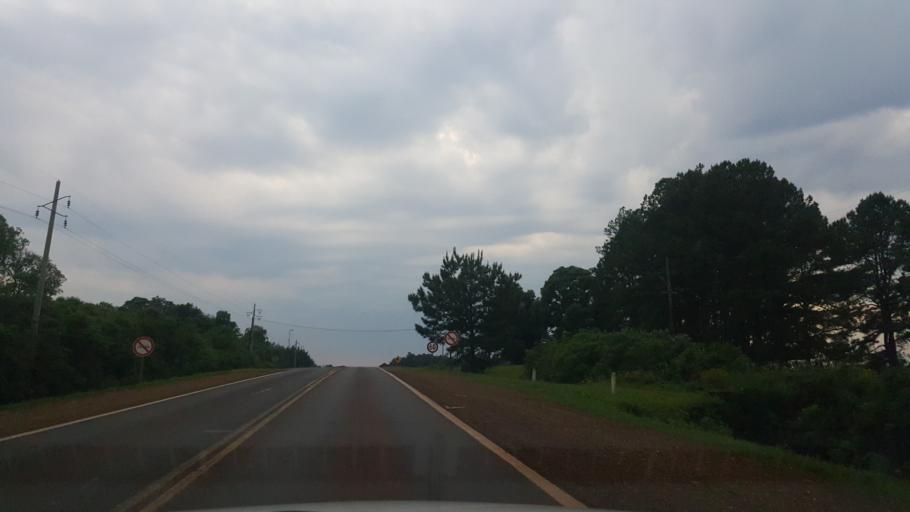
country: AR
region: Misiones
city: Jardin America
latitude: -27.0160
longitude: -55.1928
